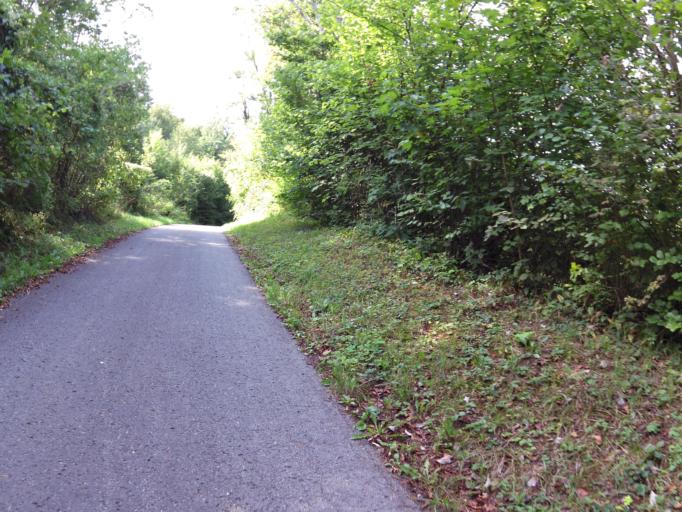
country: DE
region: Baden-Wuerttemberg
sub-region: Karlsruhe Region
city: Horb am Neckar
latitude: 48.4516
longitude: 8.7424
